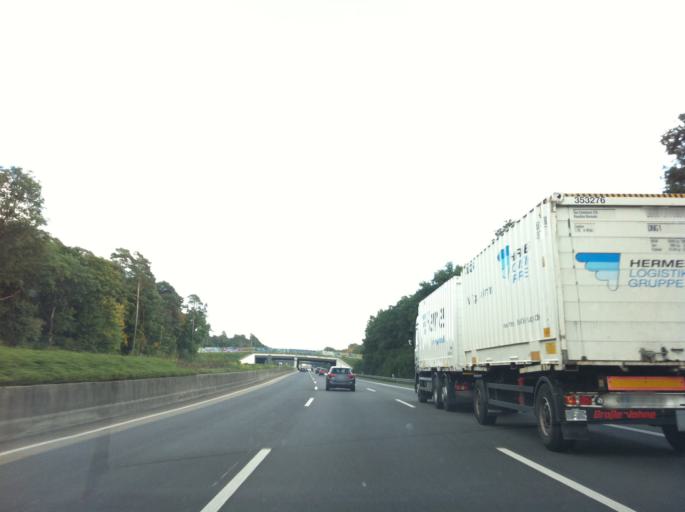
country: DE
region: North Rhine-Westphalia
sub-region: Regierungsbezirk Koln
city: Rath
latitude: 50.9079
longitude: 7.1174
